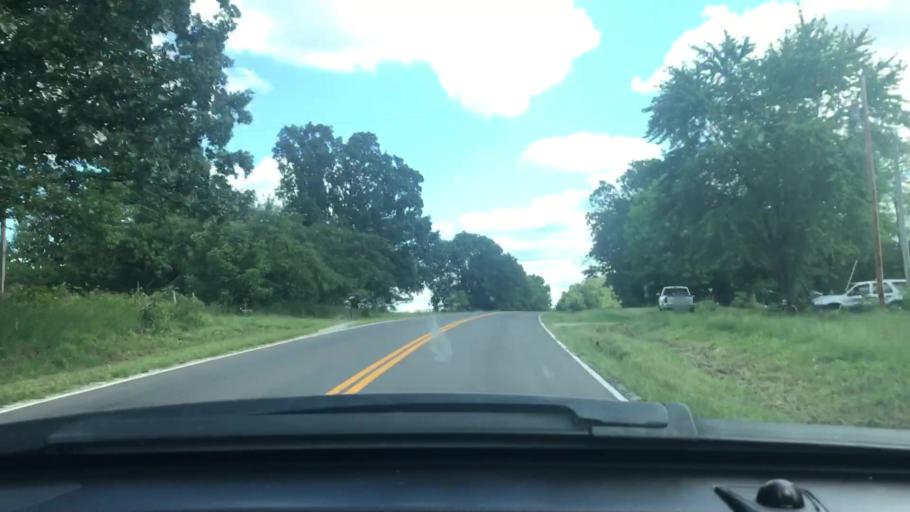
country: US
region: Missouri
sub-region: Wright County
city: Hartville
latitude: 37.3617
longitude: -92.3445
